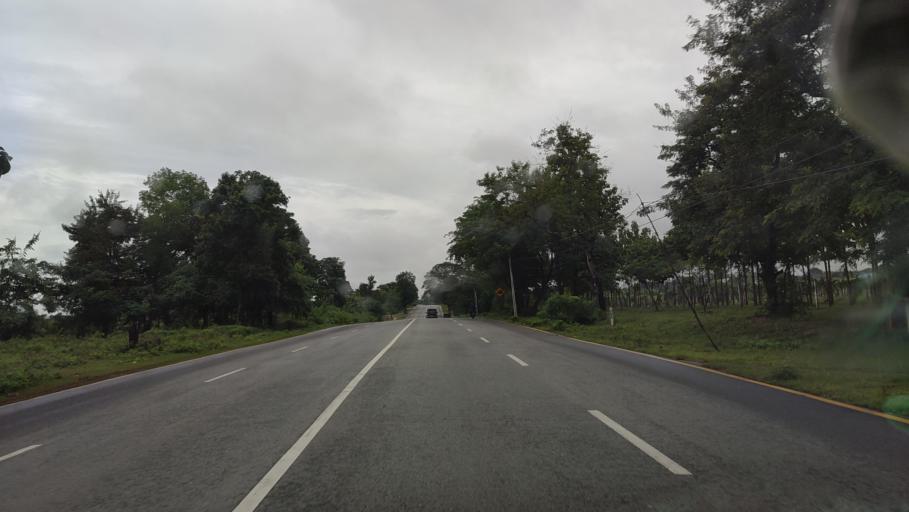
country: MM
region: Mandalay
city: Pyinmana
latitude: 19.9824
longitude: 96.2501
